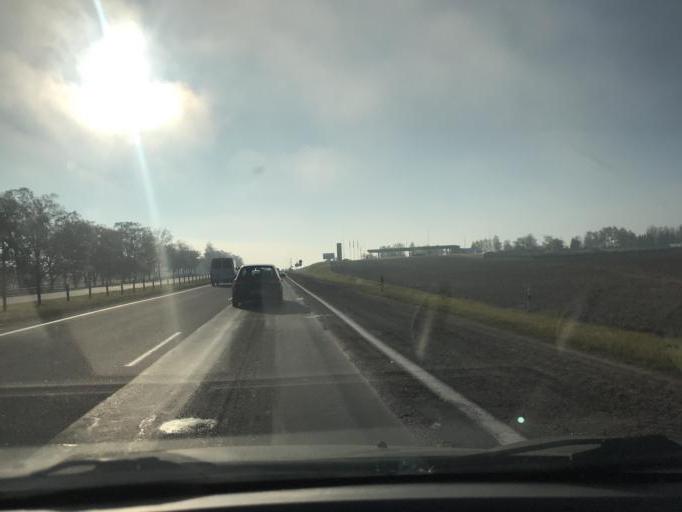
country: BY
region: Minsk
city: Dukora
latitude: 53.7087
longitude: 27.8748
